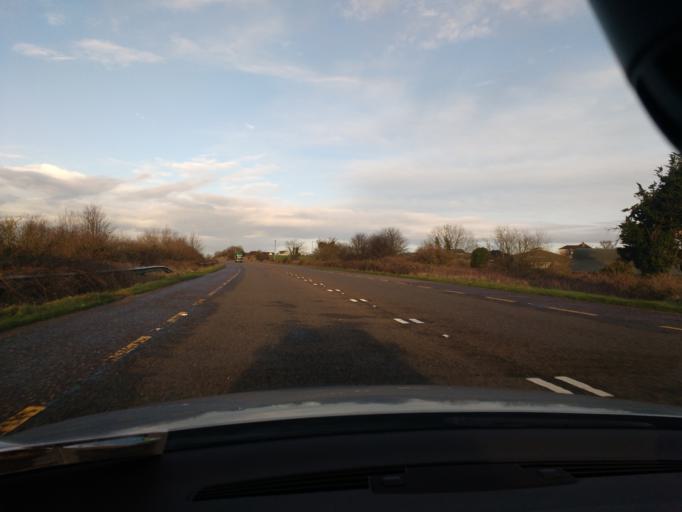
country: IE
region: Munster
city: Thurles
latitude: 52.6780
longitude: -7.6707
